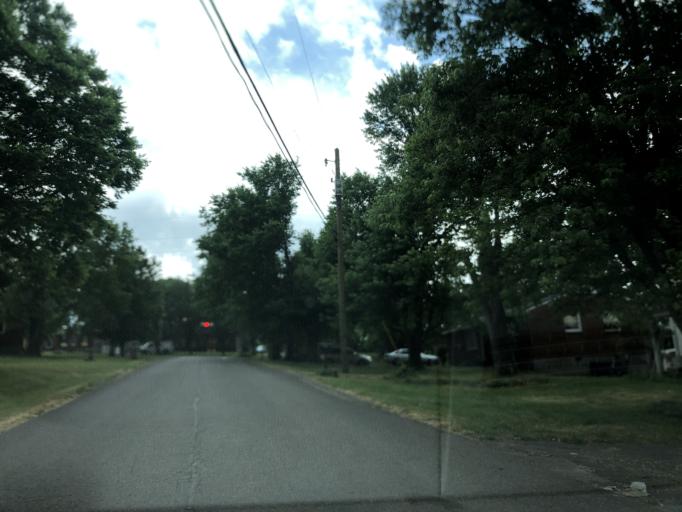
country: US
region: Tennessee
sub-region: Davidson County
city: Goodlettsville
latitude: 36.2737
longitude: -86.6985
